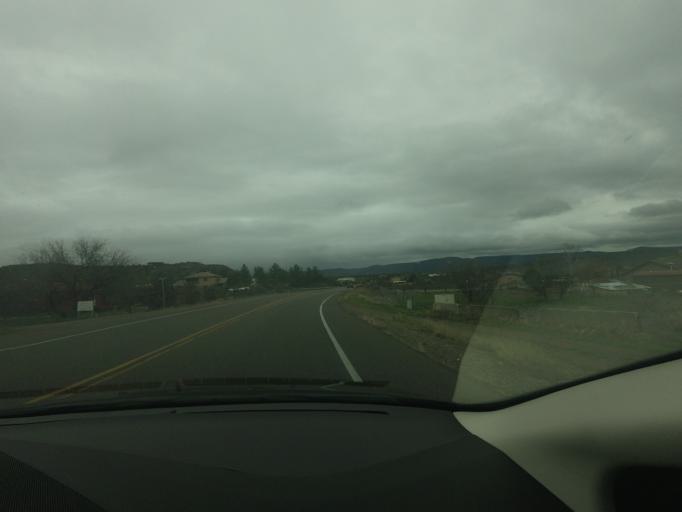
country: US
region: Arizona
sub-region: Yavapai County
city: Lake Montezuma
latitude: 34.6552
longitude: -111.7753
